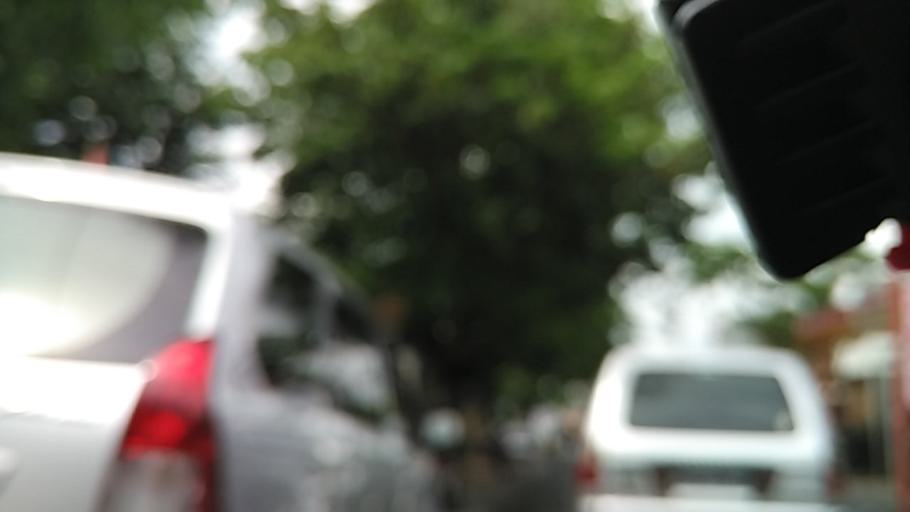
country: ID
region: Central Java
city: Semarang
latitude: -7.0071
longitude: 110.4272
